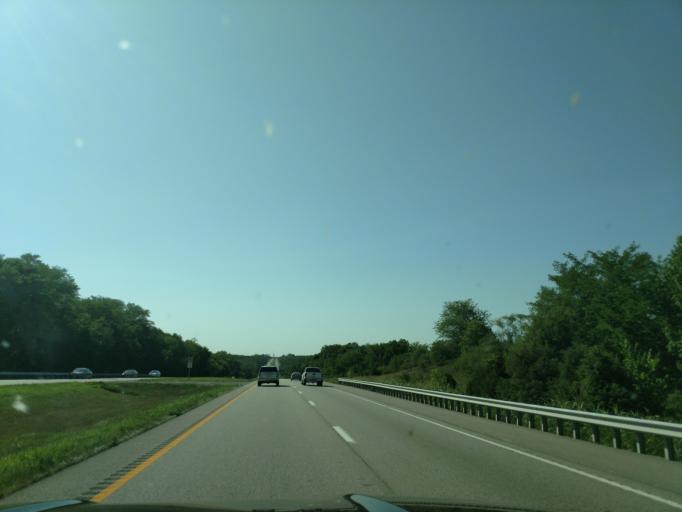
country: US
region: Missouri
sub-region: Andrew County
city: Savannah
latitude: 39.8969
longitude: -94.8735
